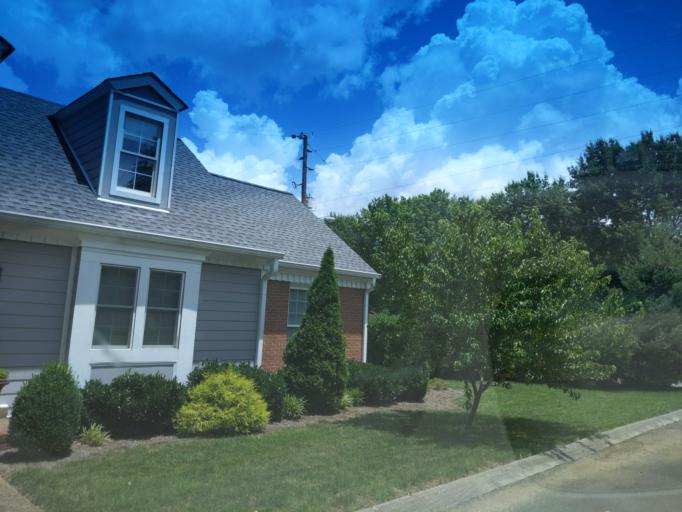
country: US
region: Tennessee
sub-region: Williamson County
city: Brentwood
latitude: 36.0382
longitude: -86.7741
